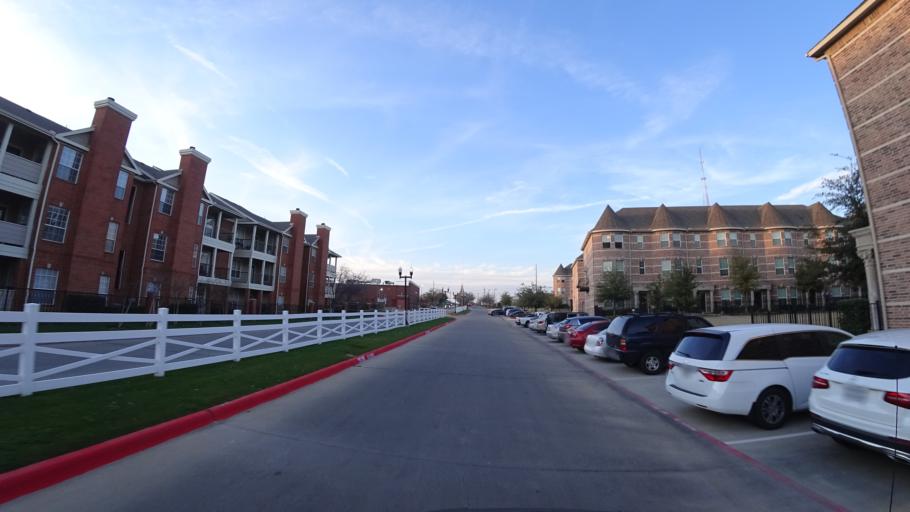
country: US
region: Texas
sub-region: Denton County
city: Lewisville
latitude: 33.0023
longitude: -96.9843
